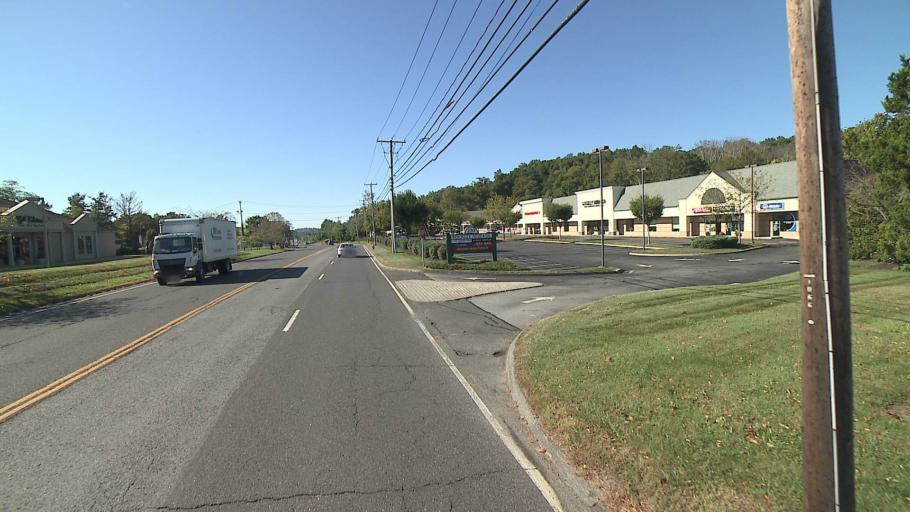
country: US
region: Connecticut
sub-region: Fairfield County
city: Danbury
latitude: 41.4480
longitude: -73.4032
